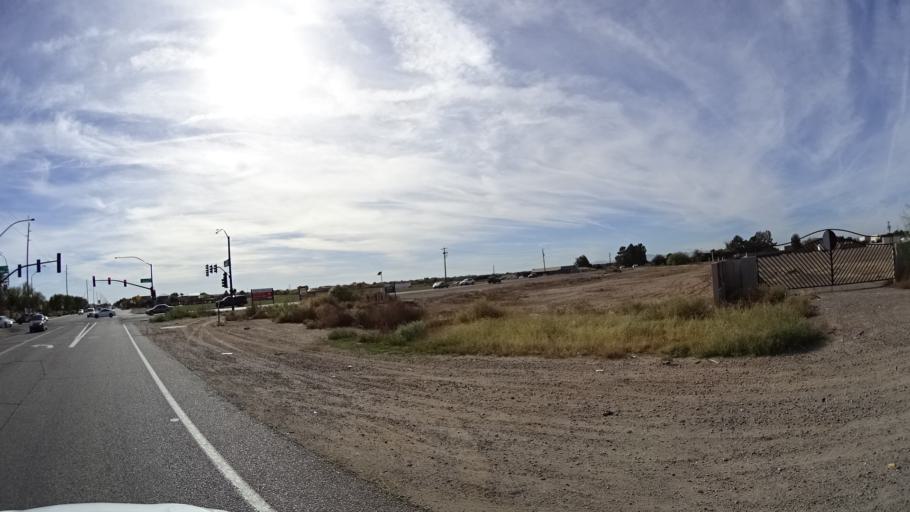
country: US
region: Arizona
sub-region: Maricopa County
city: Chandler
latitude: 33.2782
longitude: -111.7728
